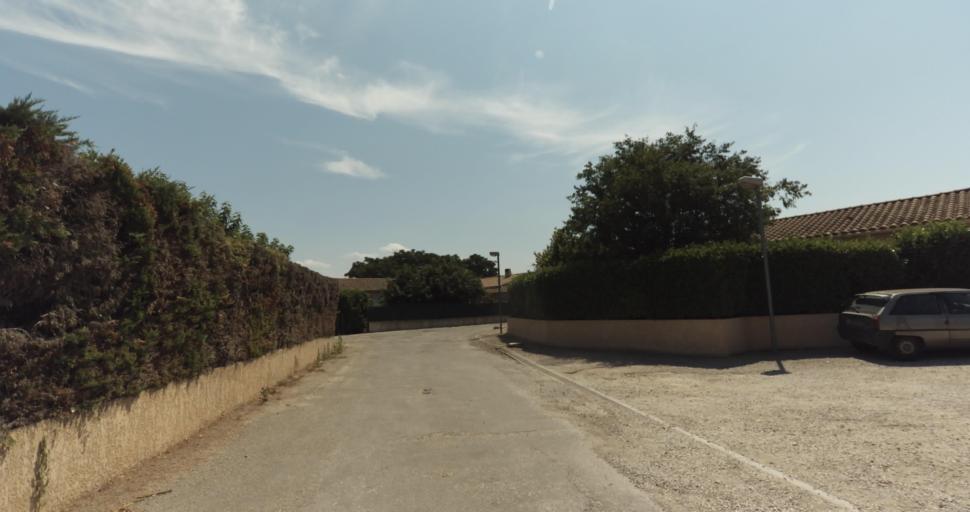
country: FR
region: Provence-Alpes-Cote d'Azur
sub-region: Departement du Vaucluse
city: Monteux
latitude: 44.0294
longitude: 4.9833
